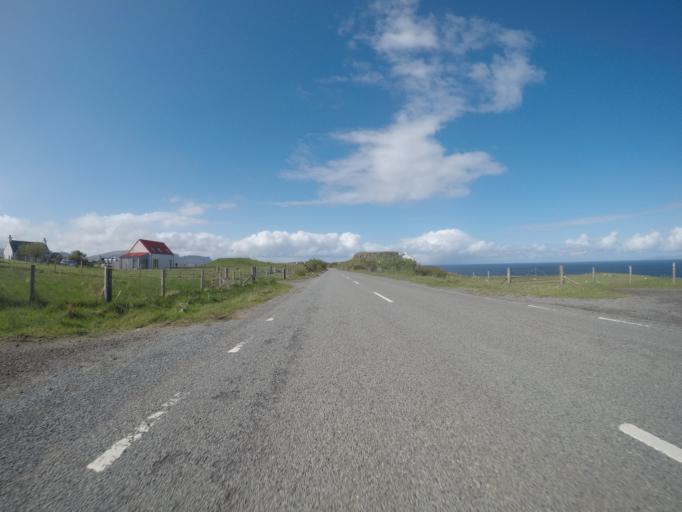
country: GB
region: Scotland
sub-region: Highland
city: Portree
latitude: 57.5964
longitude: -6.1616
